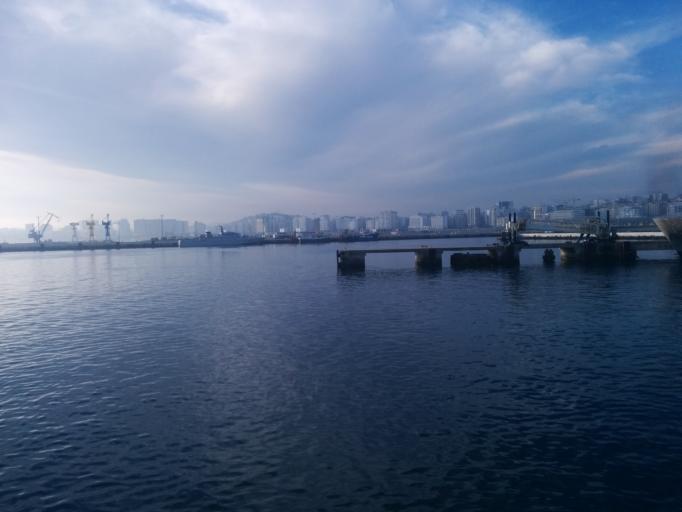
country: MA
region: Tanger-Tetouan
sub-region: Tanger-Assilah
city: Tangier
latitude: 35.7909
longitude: -5.8024
